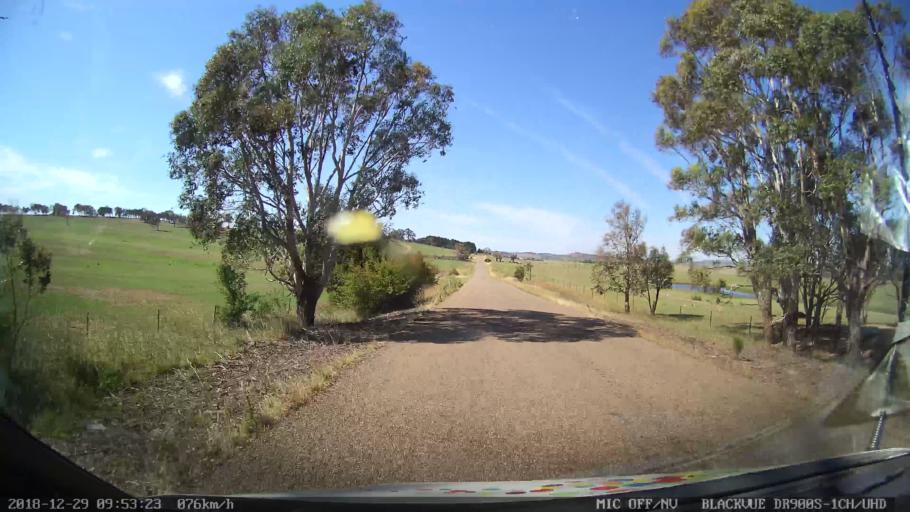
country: AU
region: New South Wales
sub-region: Goulburn Mulwaree
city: Goulburn
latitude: -34.7509
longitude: 149.4696
